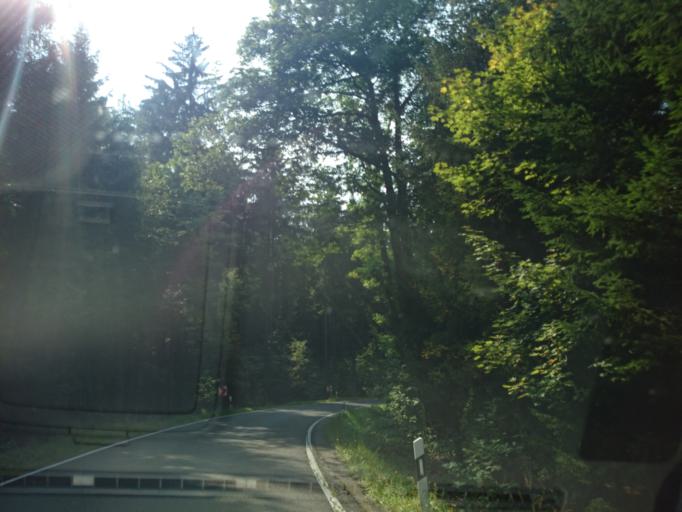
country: DE
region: Saxony
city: Augustusburg
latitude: 50.7902
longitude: 13.1045
